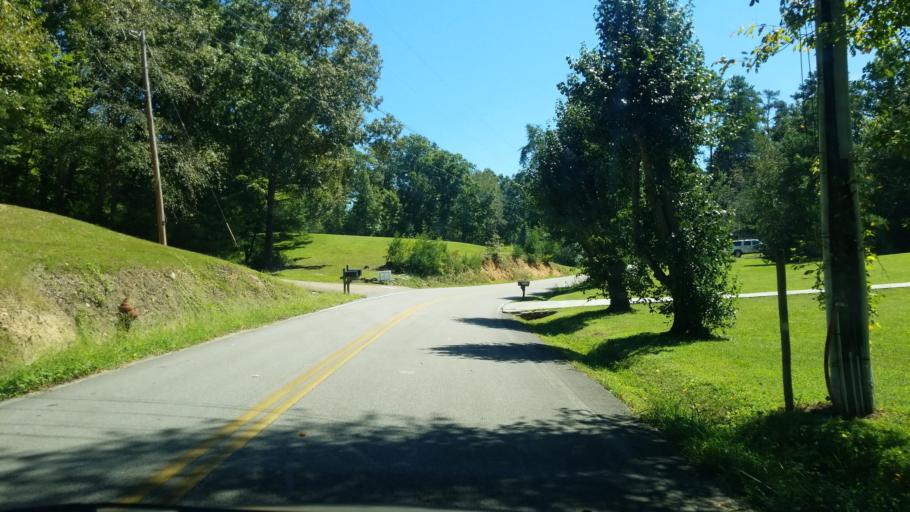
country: US
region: Tennessee
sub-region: Hamilton County
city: Harrison
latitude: 35.0978
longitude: -85.0847
